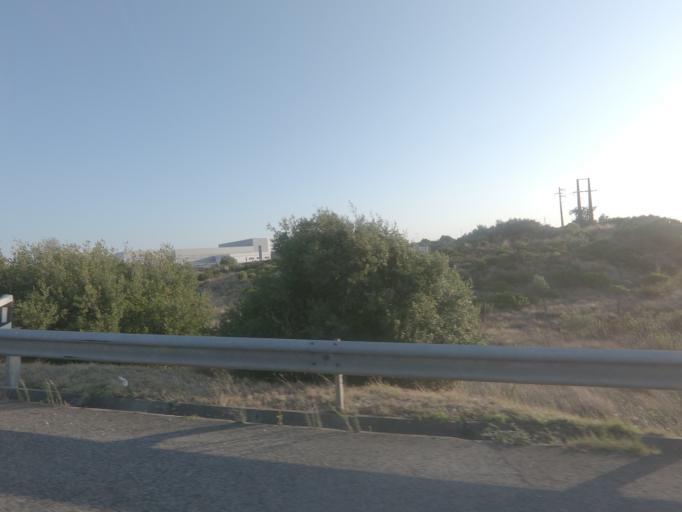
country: PT
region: Santarem
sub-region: Alcanena
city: Alcanena
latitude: 39.4810
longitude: -8.6234
